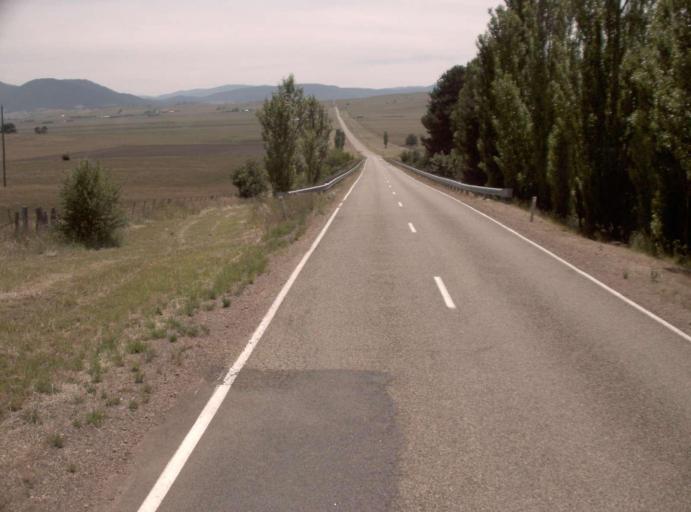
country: AU
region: Victoria
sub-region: Alpine
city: Mount Beauty
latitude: -37.0050
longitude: 147.6631
